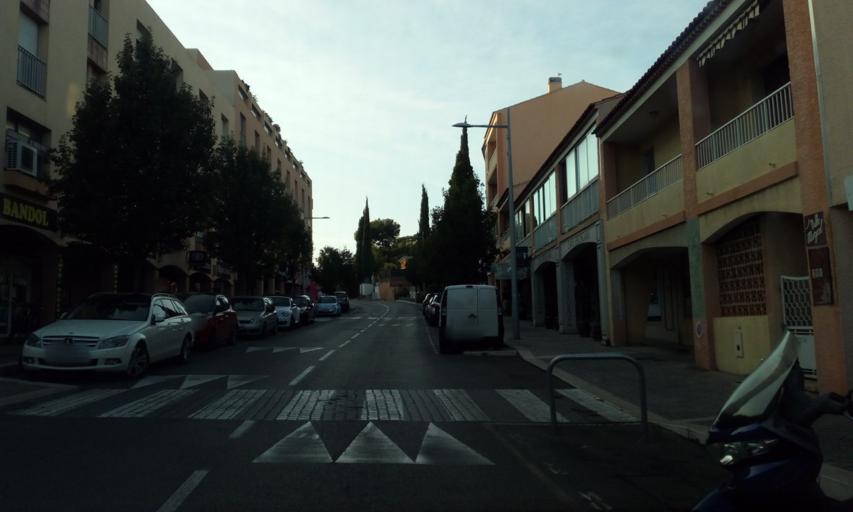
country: FR
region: Provence-Alpes-Cote d'Azur
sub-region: Departement du Var
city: Bandol
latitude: 43.1380
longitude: 5.7518
